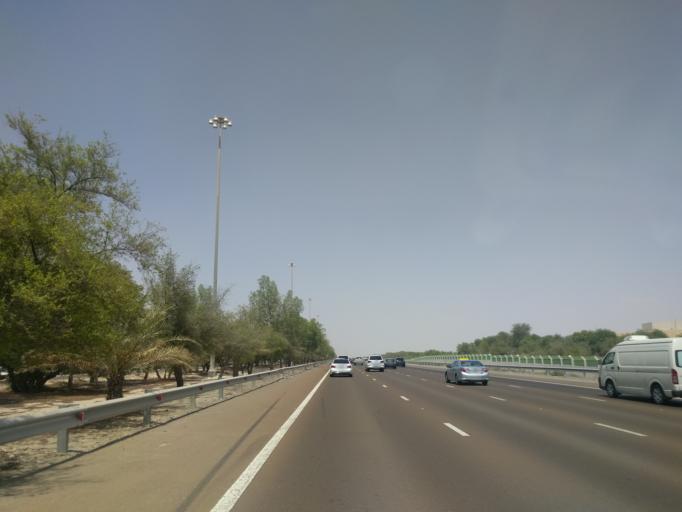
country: AE
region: Abu Dhabi
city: Abu Dhabi
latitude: 24.7143
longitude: 54.7996
